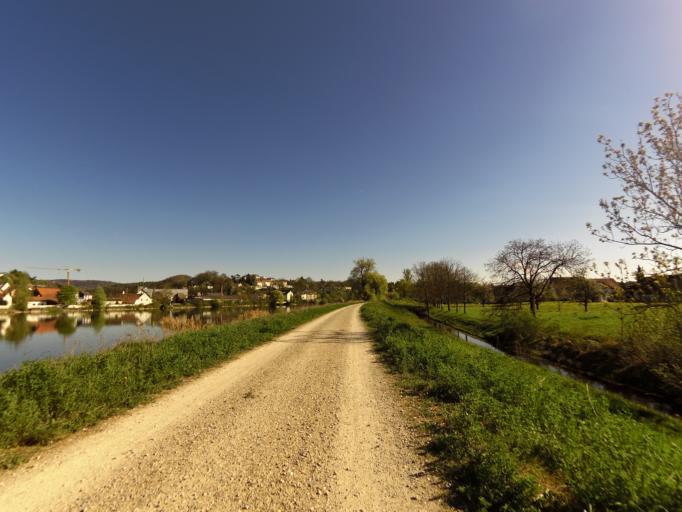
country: CH
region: Aargau
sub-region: Bezirk Zurzach
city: Klingnau
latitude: 47.5714
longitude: 8.2524
